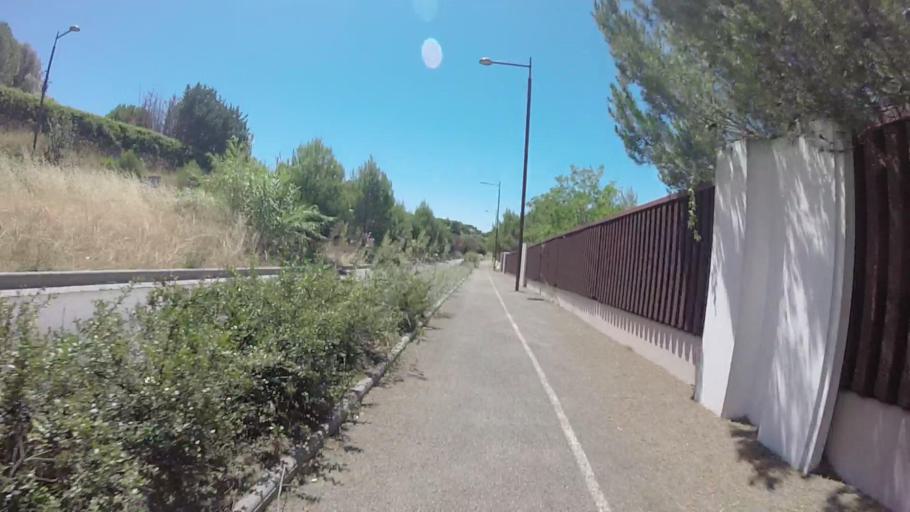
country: FR
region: Provence-Alpes-Cote d'Azur
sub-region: Departement des Alpes-Maritimes
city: Biot
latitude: 43.5912
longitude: 7.0920
